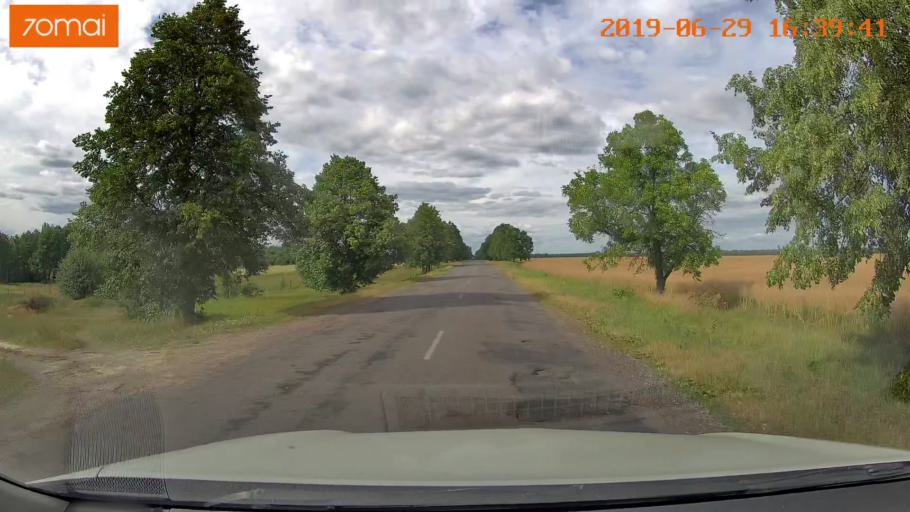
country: BY
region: Brest
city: Luninyets
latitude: 52.2454
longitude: 27.0165
